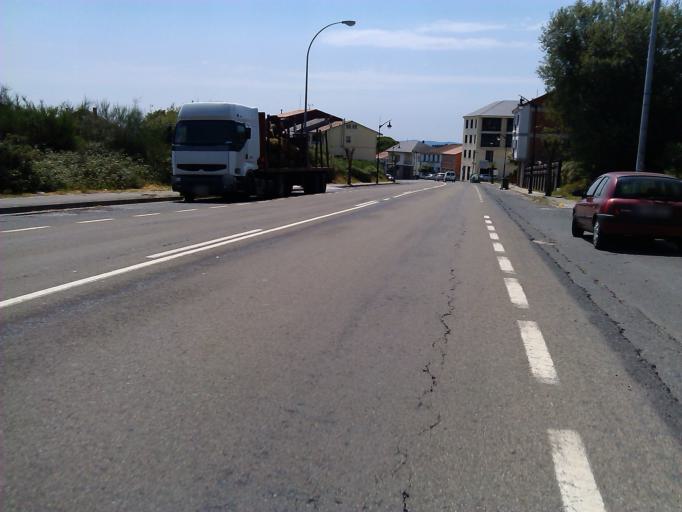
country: ES
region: Galicia
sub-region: Provincia de Lugo
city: Monterroso
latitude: 42.8757
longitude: -7.8649
